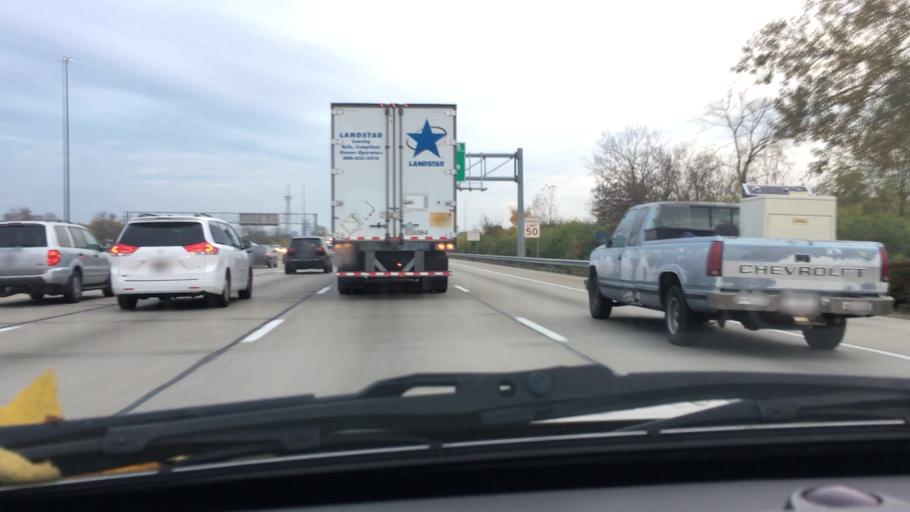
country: US
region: Indiana
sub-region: Marion County
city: Warren Park
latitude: 39.8007
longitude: -86.0938
